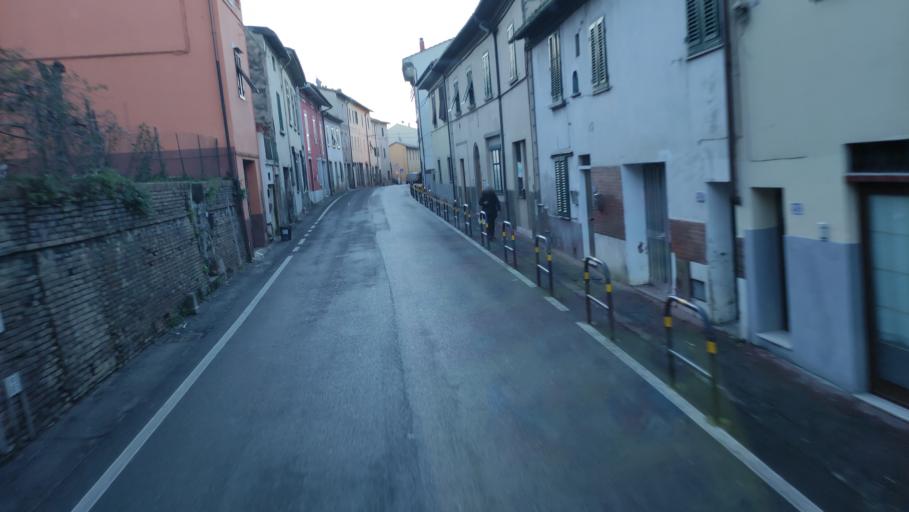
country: IT
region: Tuscany
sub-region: Province of Florence
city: Pozzale-Case Nuove
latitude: 43.6557
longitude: 10.9416
